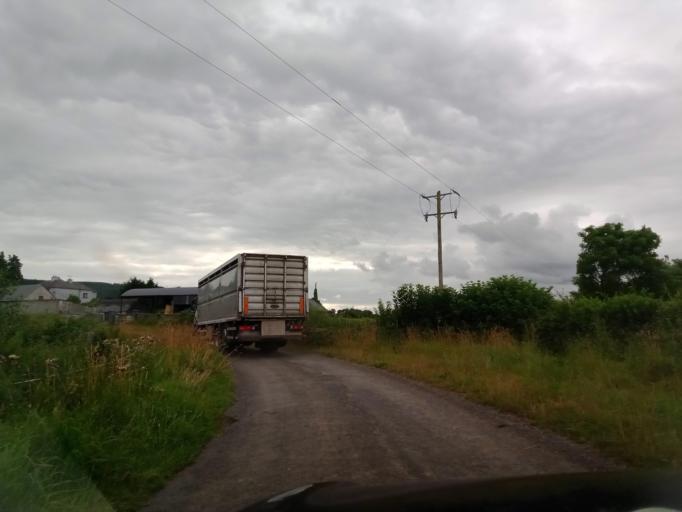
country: IE
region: Leinster
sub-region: Laois
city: Stradbally
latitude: 52.9640
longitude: -7.1658
